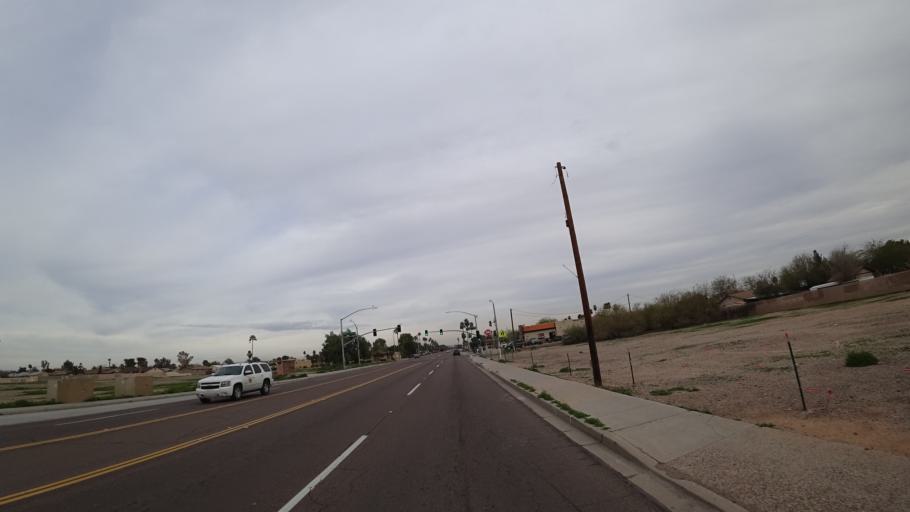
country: US
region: Arizona
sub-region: Maricopa County
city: Peoria
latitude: 33.5808
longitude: -112.2516
